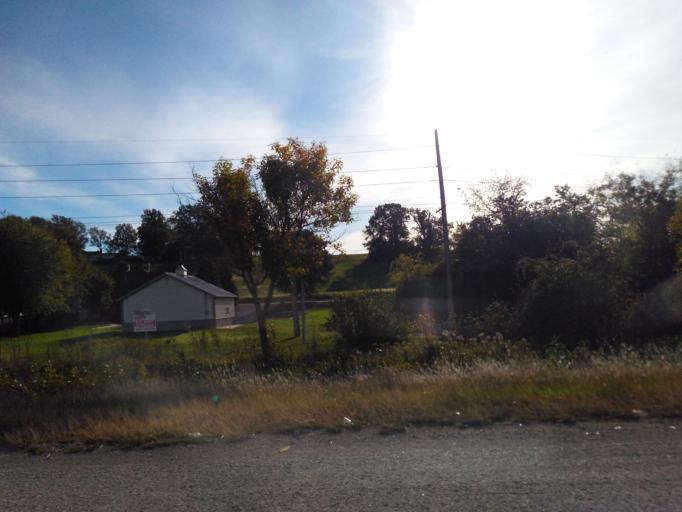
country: US
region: Illinois
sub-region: Saint Clair County
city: Dupo
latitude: 38.4864
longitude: -90.2196
